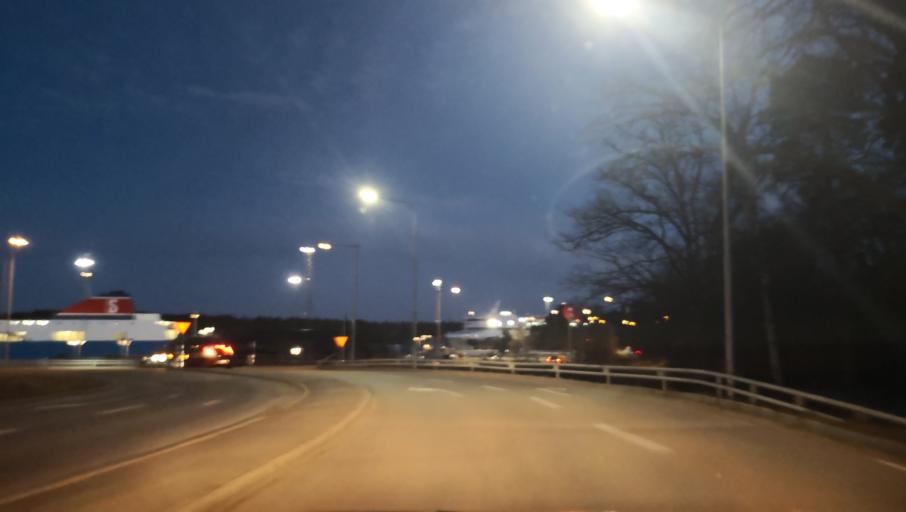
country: SE
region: Stockholm
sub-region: Nynashamns Kommun
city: Nynashamn
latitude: 58.9091
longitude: 17.9541
